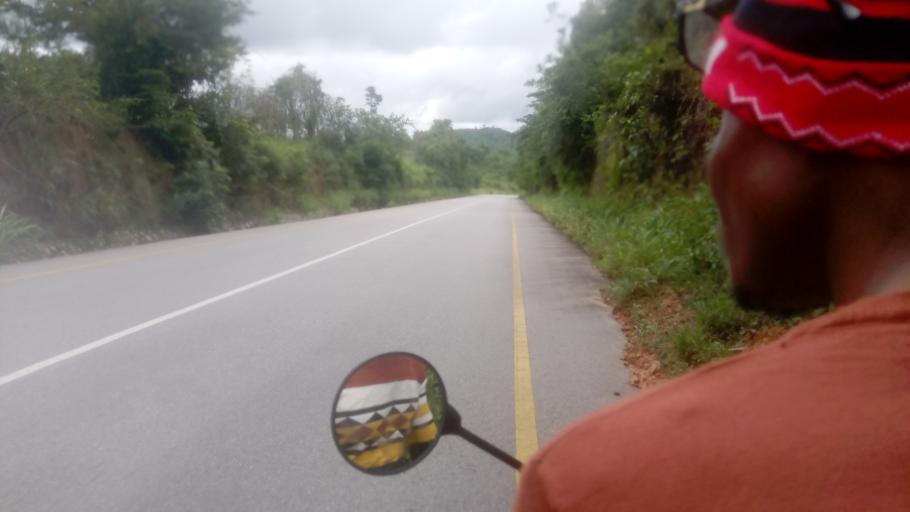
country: SL
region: Northern Province
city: Masaka
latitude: 8.6456
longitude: -11.7518
